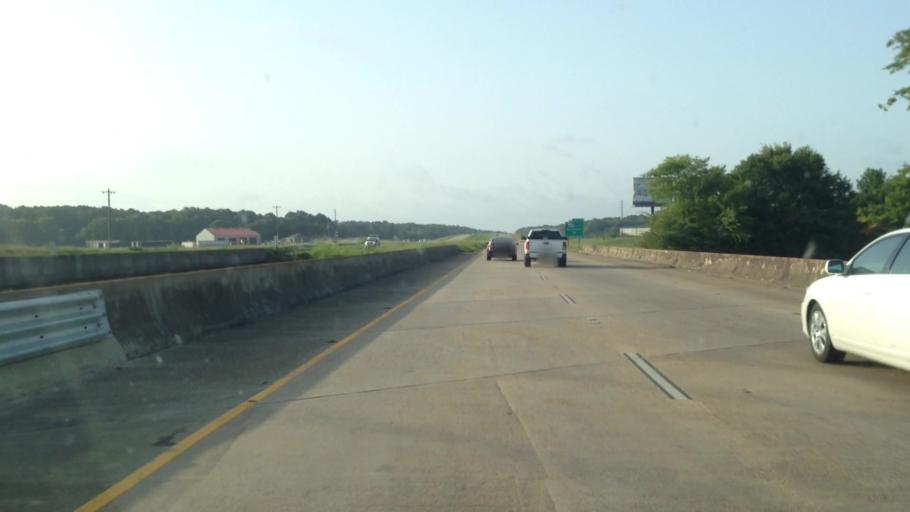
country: US
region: Louisiana
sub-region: Rapides Parish
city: Woodworth
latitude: 31.1721
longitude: -92.4641
